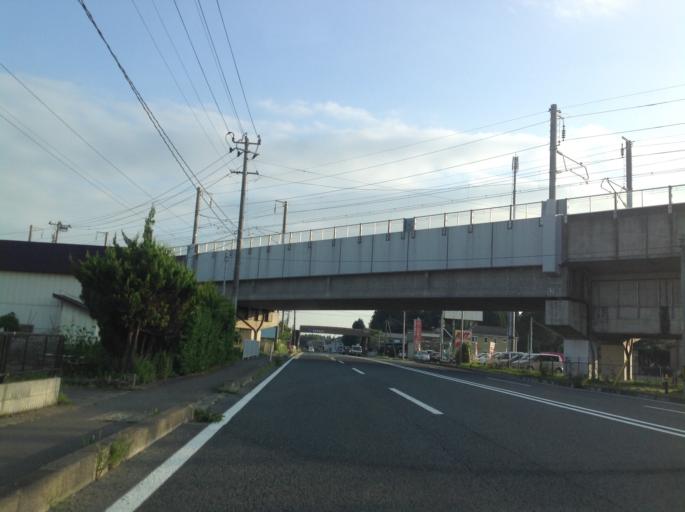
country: JP
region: Iwate
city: Hanamaki
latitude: 39.5367
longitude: 141.1674
